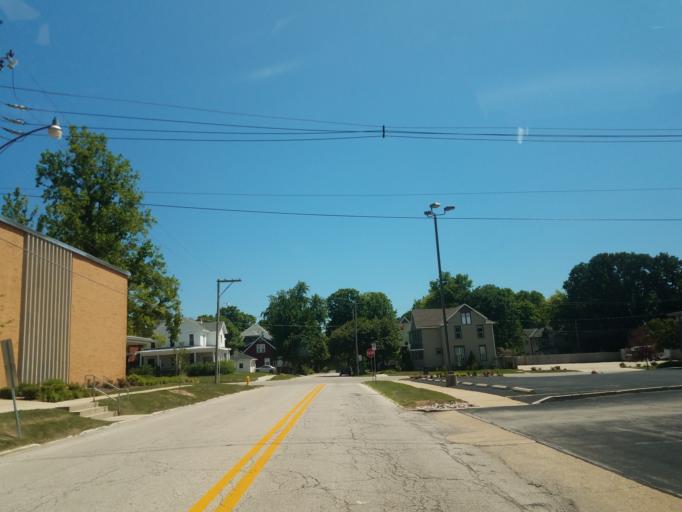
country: US
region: Illinois
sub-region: McLean County
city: Bloomington
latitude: 40.4793
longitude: -88.9885
